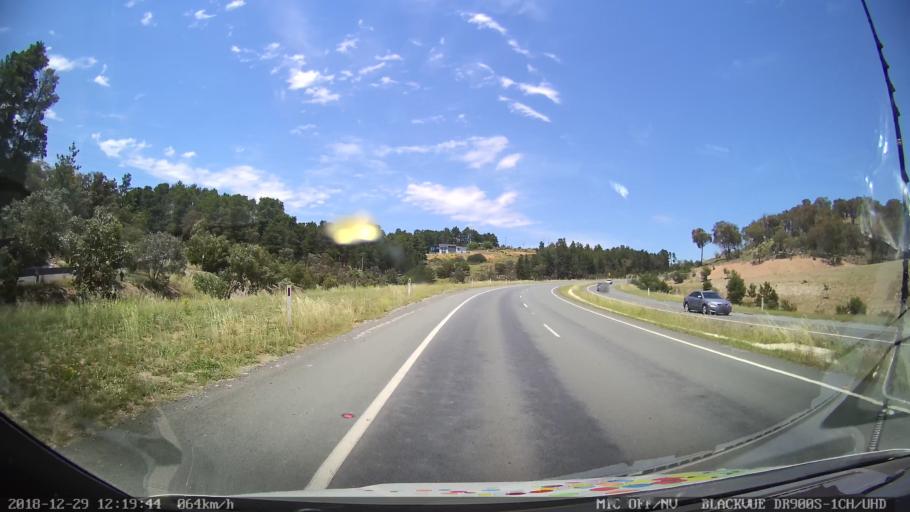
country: AU
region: New South Wales
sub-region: Queanbeyan
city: Queanbeyan
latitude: -35.3965
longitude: 149.2335
